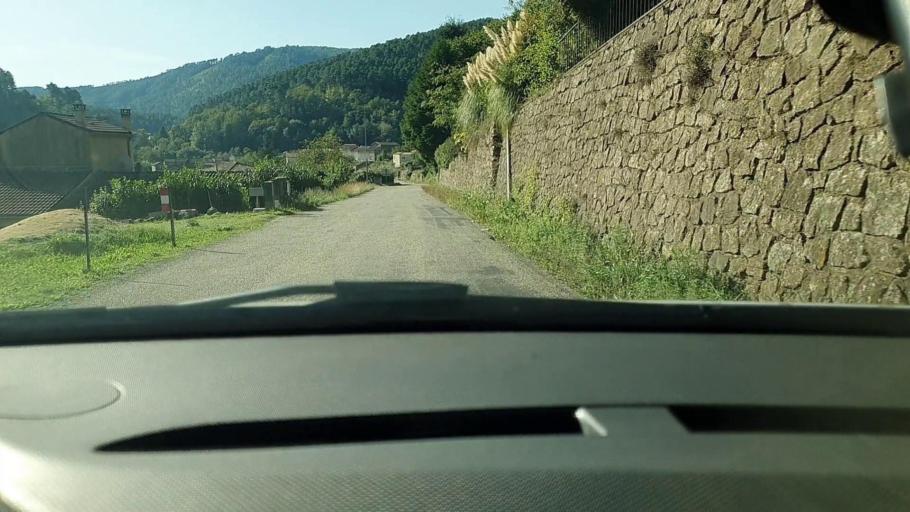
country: FR
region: Languedoc-Roussillon
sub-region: Departement du Gard
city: Besseges
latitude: 44.3070
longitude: 4.0594
